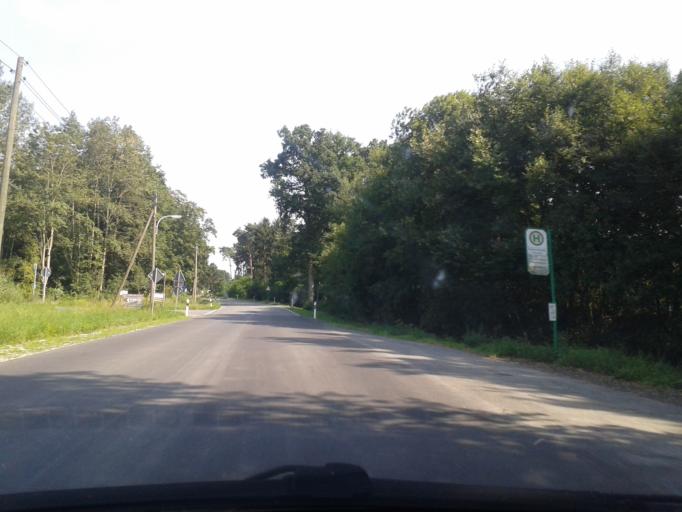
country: DE
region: North Rhine-Westphalia
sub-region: Regierungsbezirk Detmold
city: Hovelhof
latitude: 51.8510
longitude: 8.5866
